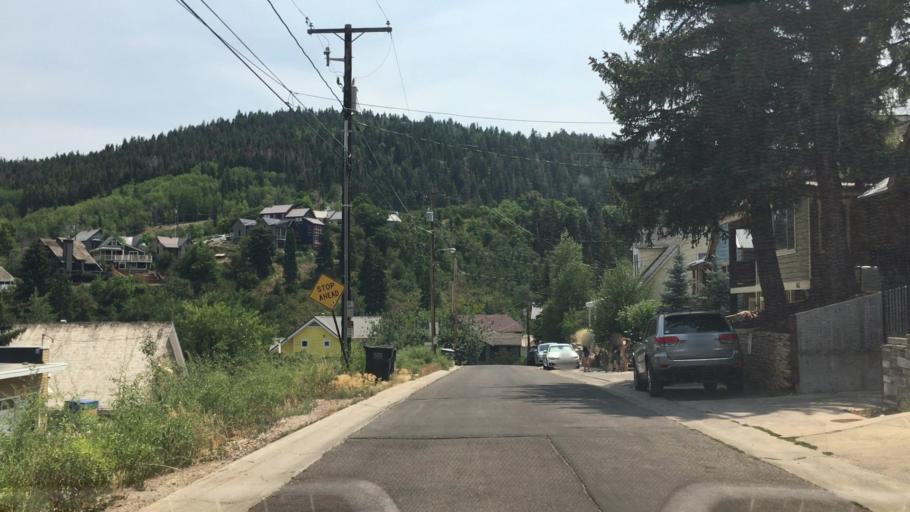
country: US
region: Utah
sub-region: Summit County
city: Park City
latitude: 40.6404
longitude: -111.4956
